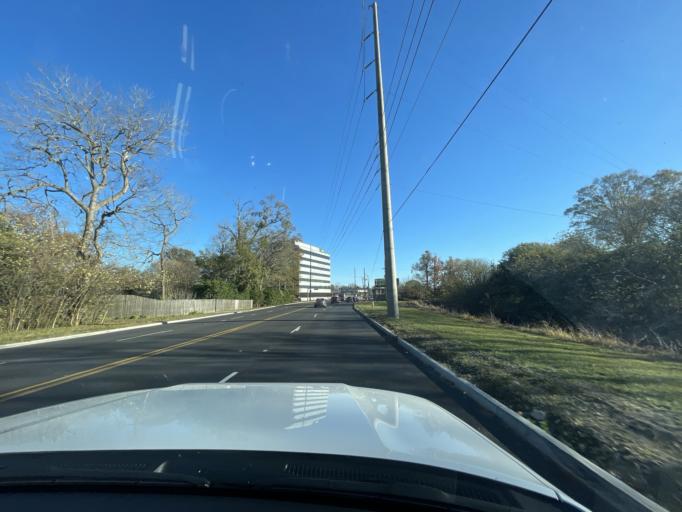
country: US
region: Louisiana
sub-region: East Baton Rouge Parish
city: Baton Rouge
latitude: 30.4278
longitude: -91.1520
